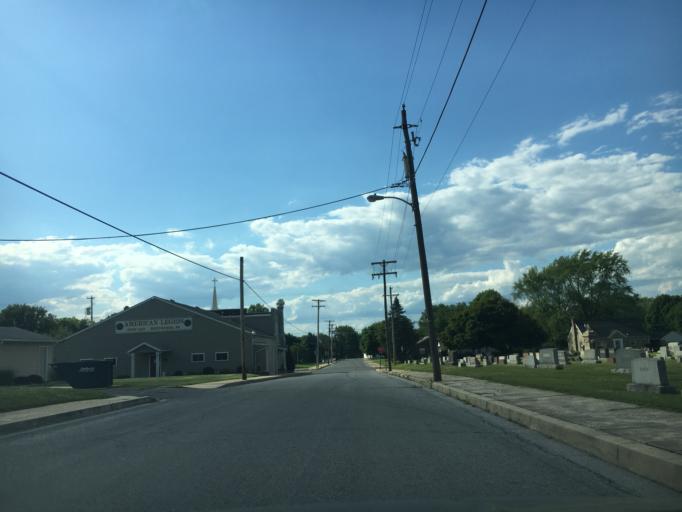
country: US
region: Pennsylvania
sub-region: Berks County
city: Fleetwood
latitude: 40.4568
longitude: -75.8165
